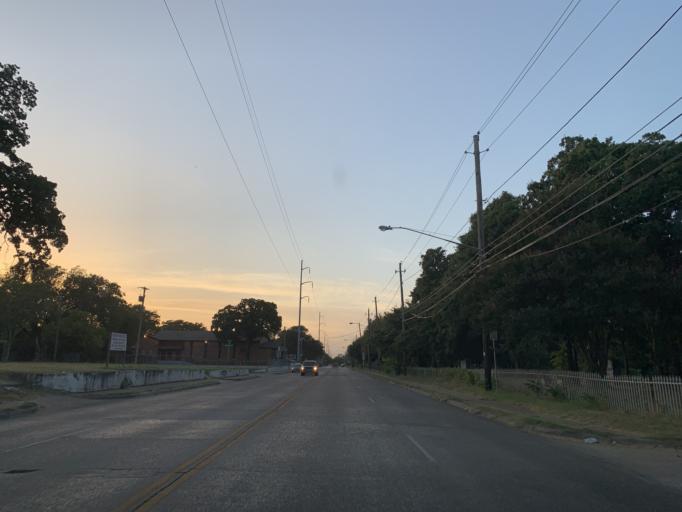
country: US
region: Texas
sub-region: Dallas County
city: Dallas
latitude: 32.7612
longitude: -96.7591
